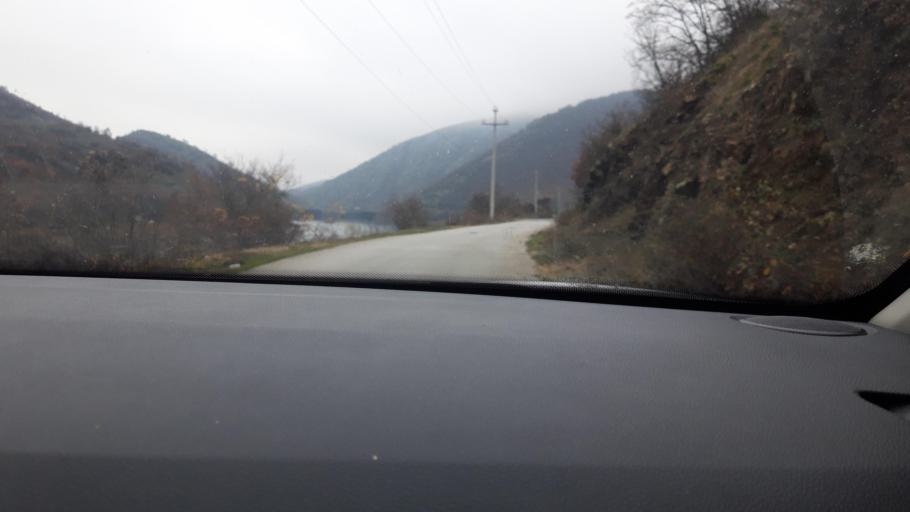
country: MK
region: Opstina Lipkovo
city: Lipkovo
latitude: 42.1725
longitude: 21.5693
